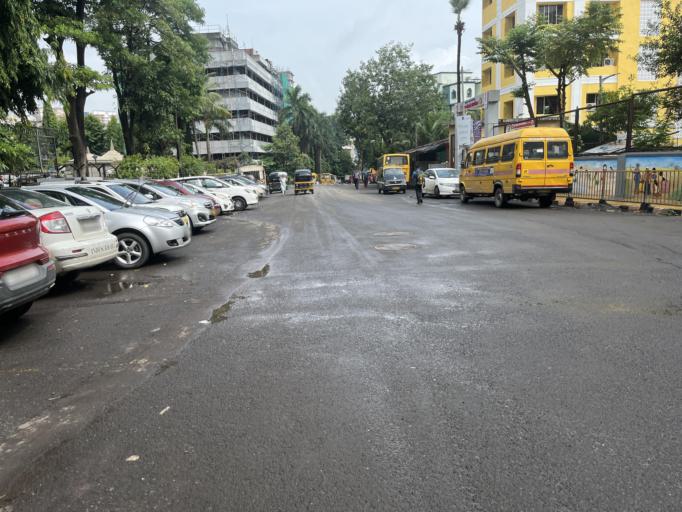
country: IN
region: Maharashtra
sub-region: Mumbai Suburban
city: Borivli
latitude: 19.2276
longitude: 72.8657
